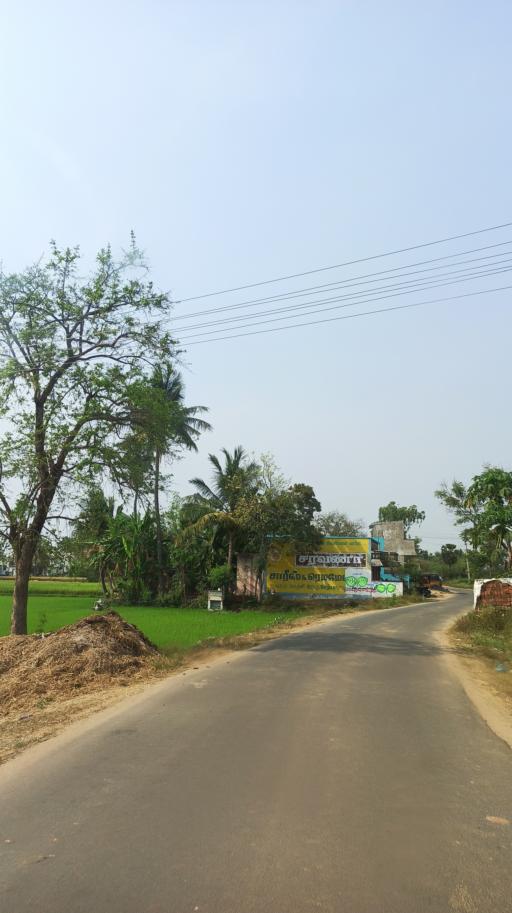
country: IN
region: Tamil Nadu
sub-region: Tiruvannamalai
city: Desur
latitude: 12.4512
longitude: 79.3723
